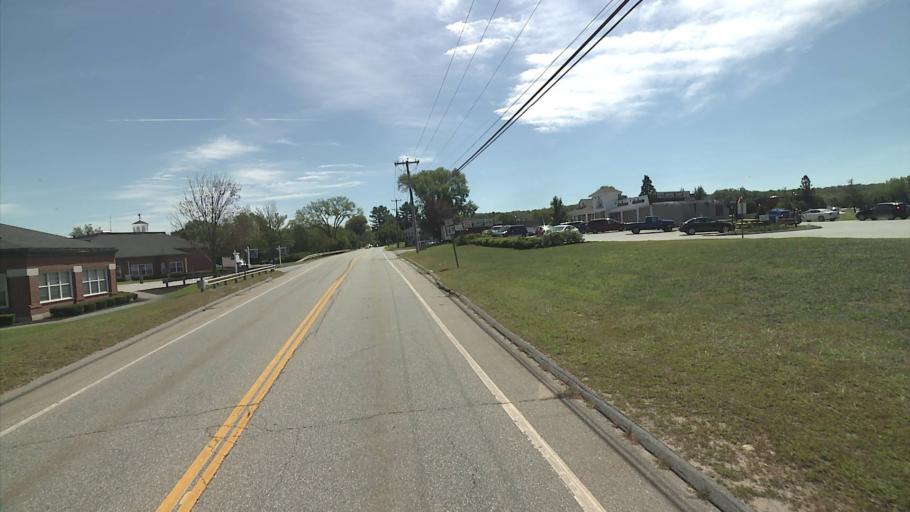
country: US
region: Connecticut
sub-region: Windham County
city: Putnam
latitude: 41.8592
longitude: -71.9613
